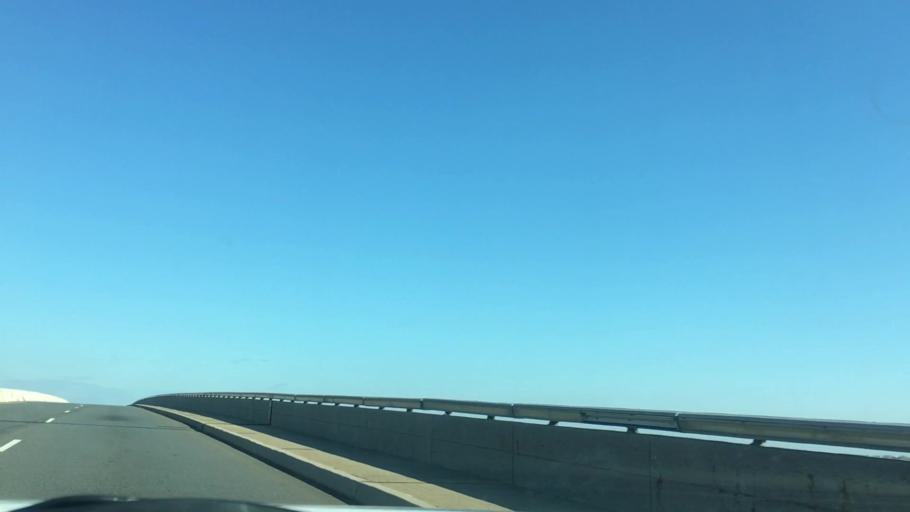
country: US
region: New Jersey
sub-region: Atlantic County
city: Atlantic City
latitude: 39.3846
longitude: -74.4230
